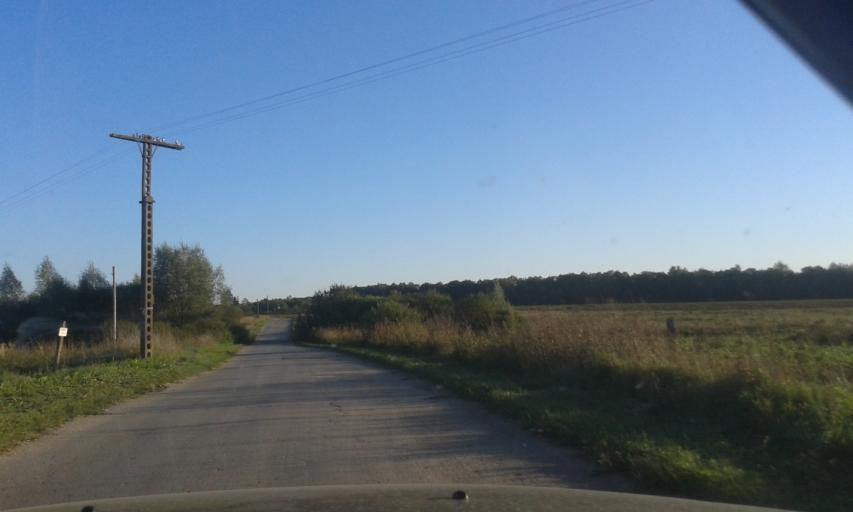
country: RU
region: Tula
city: Krapivna
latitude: 54.1196
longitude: 37.1527
